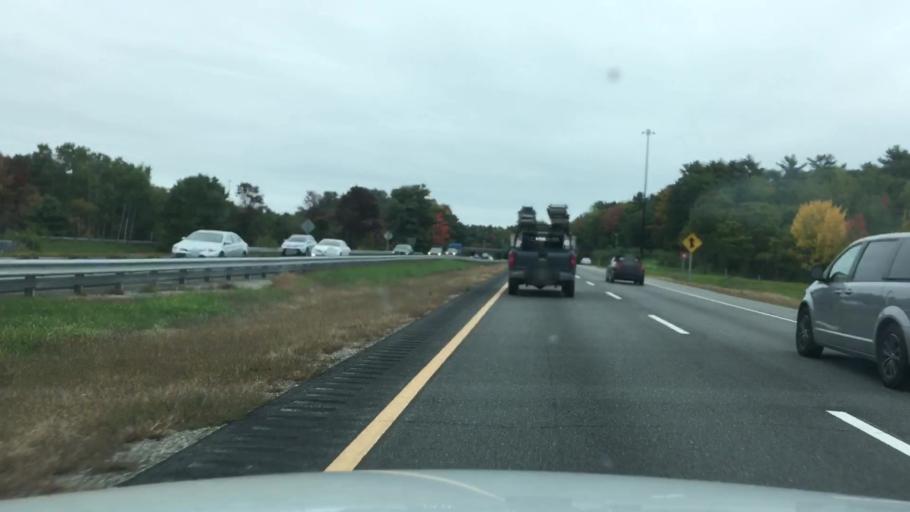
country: US
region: Maine
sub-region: Cumberland County
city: Falmouth
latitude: 43.7286
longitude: -70.2361
